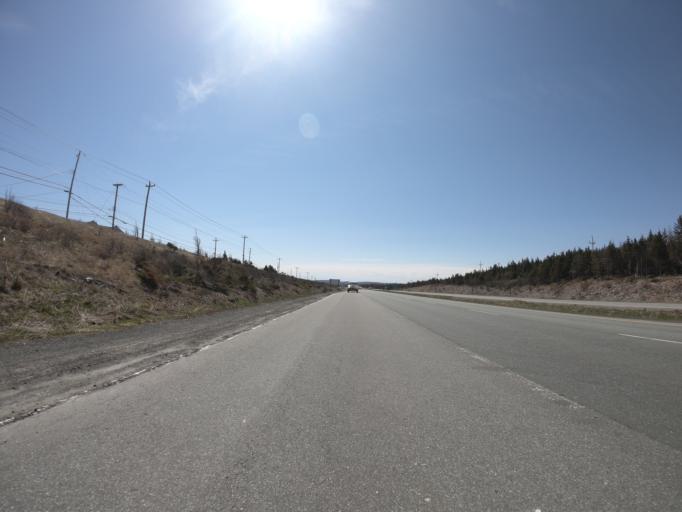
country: CA
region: Newfoundland and Labrador
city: Mount Pearl
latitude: 47.5057
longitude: -52.8214
